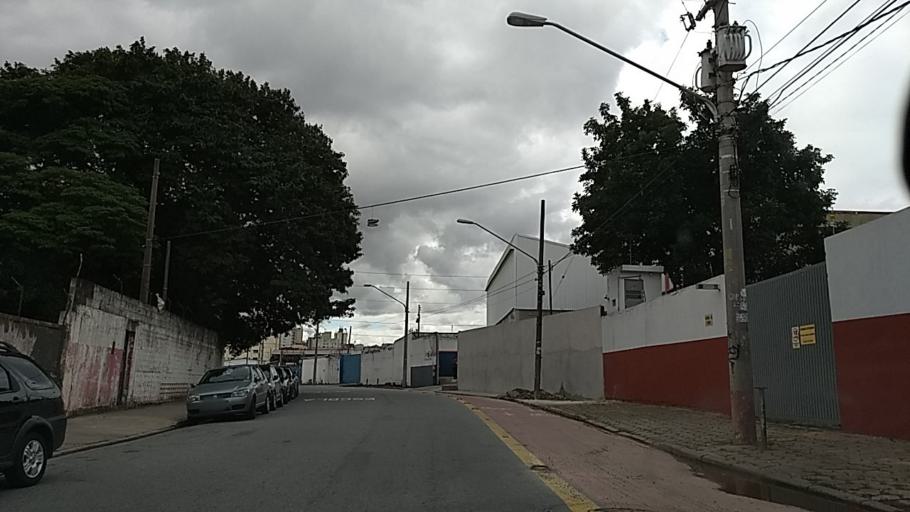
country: BR
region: Sao Paulo
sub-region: Sao Paulo
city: Sao Paulo
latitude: -23.5117
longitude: -46.6085
